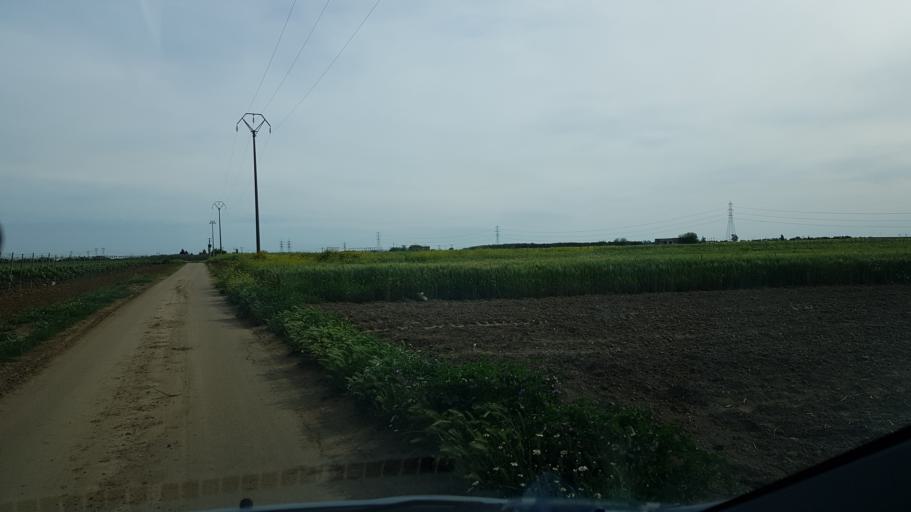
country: IT
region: Apulia
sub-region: Provincia di Brindisi
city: Tuturano
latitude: 40.5727
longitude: 17.9203
